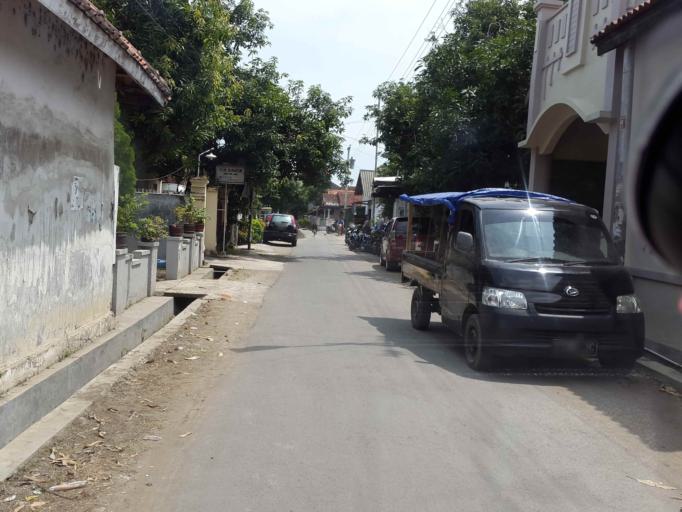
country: ID
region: Central Java
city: Petarukan
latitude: -6.8923
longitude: 109.4025
